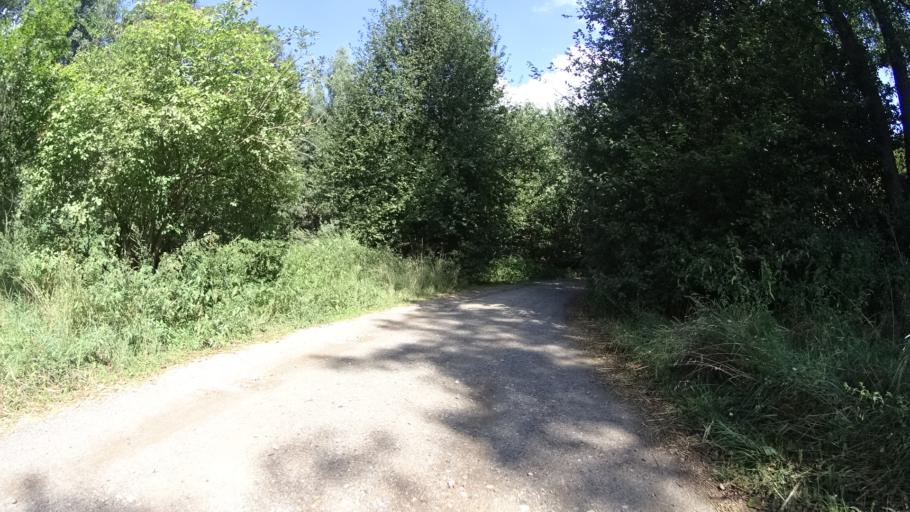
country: PL
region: Masovian Voivodeship
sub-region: Powiat grojecki
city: Mogielnica
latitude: 51.6715
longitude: 20.7455
